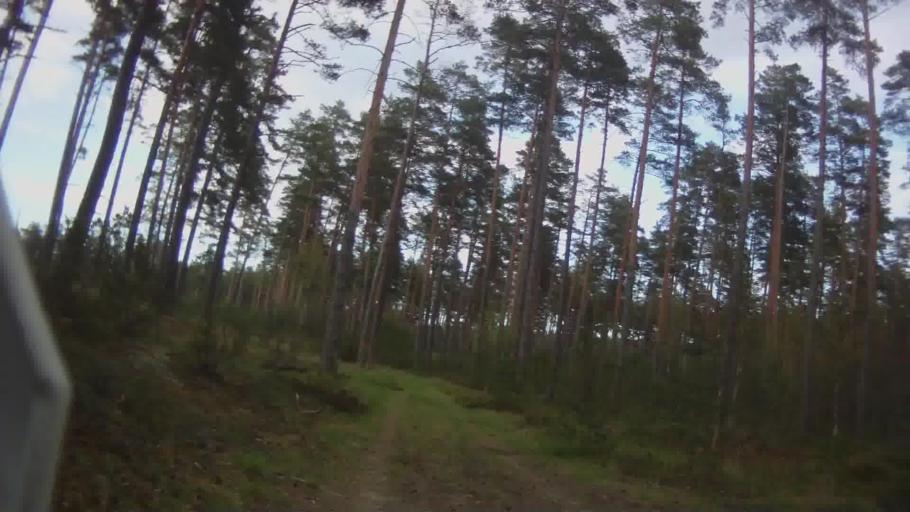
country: LV
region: Riga
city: Jaunciems
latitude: 57.0645
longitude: 24.1676
